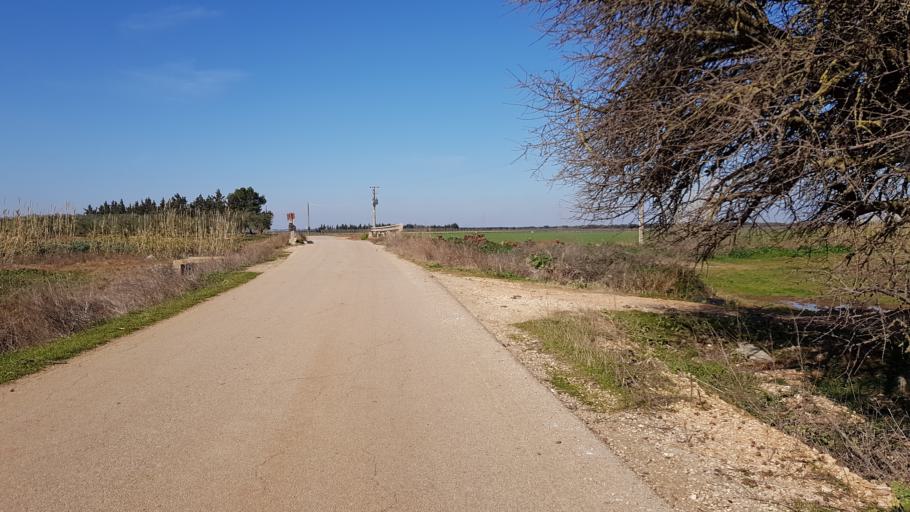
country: IT
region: Apulia
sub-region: Provincia di Brindisi
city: Mesagne
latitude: 40.6194
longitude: 17.8154
